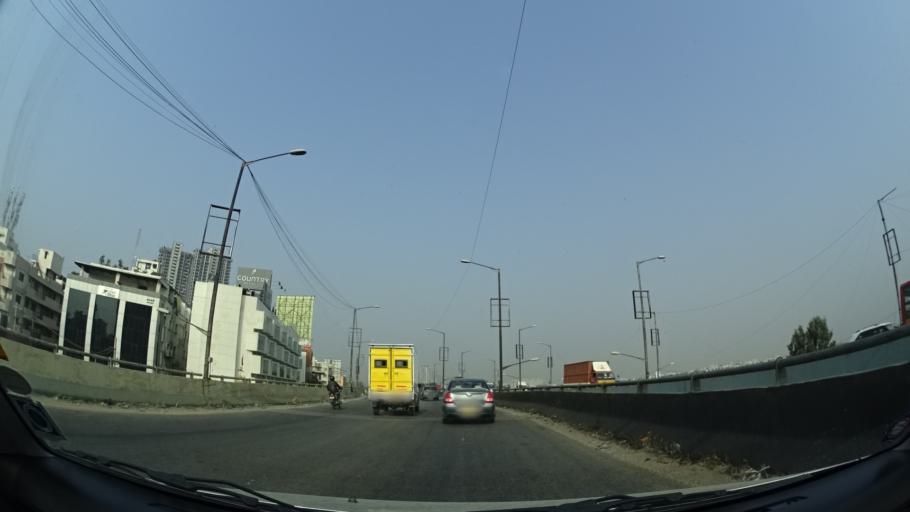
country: IN
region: Karnataka
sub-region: Bangalore Urban
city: Yelahanka
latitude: 13.0419
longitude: 77.6142
